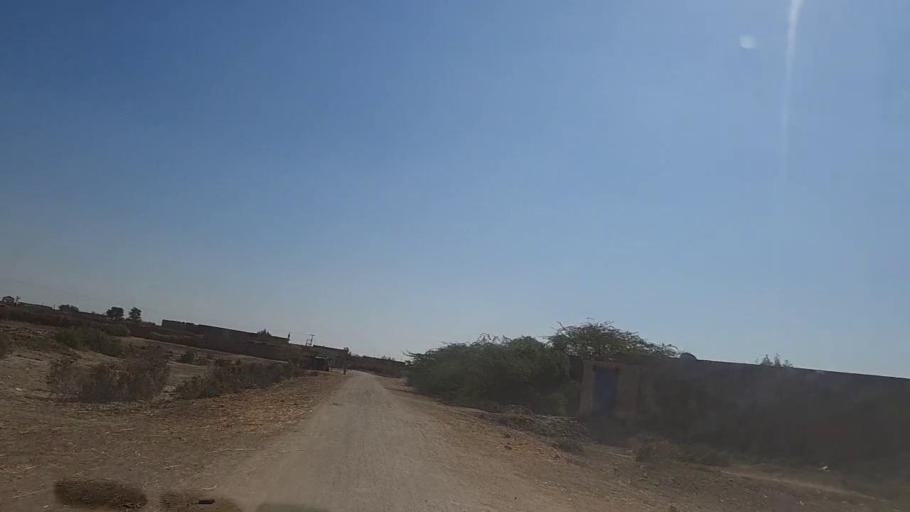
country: PK
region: Sindh
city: Digri
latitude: 25.1011
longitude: 69.1280
